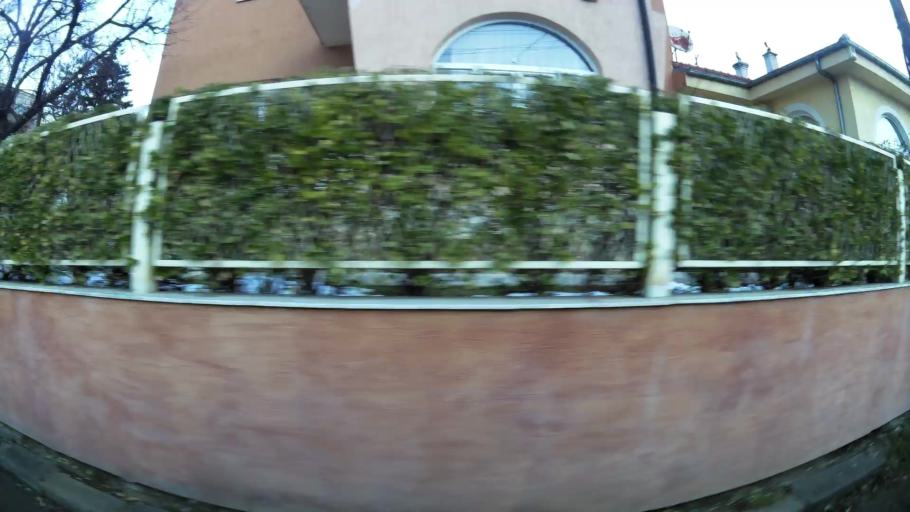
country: XK
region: Pristina
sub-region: Komuna e Prishtines
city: Pristina
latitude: 42.6668
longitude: 21.1792
